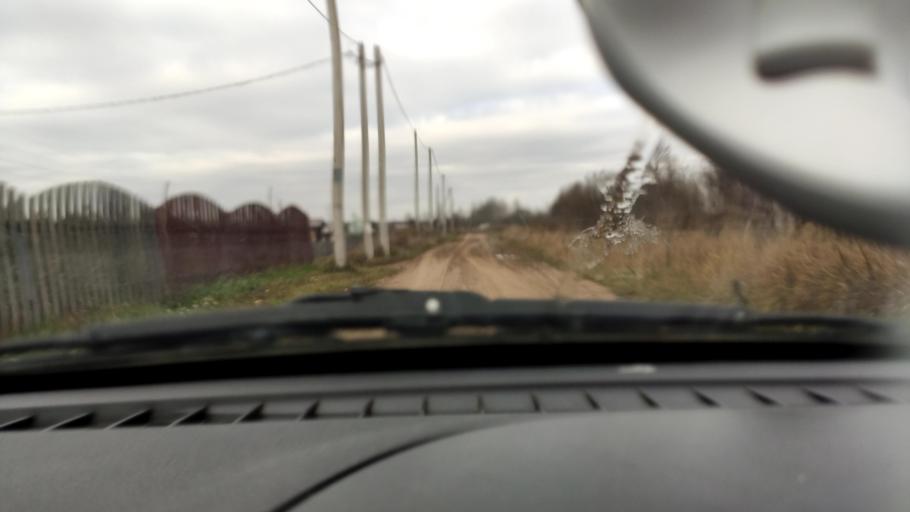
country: RU
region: Perm
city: Kondratovo
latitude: 57.9899
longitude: 56.0762
